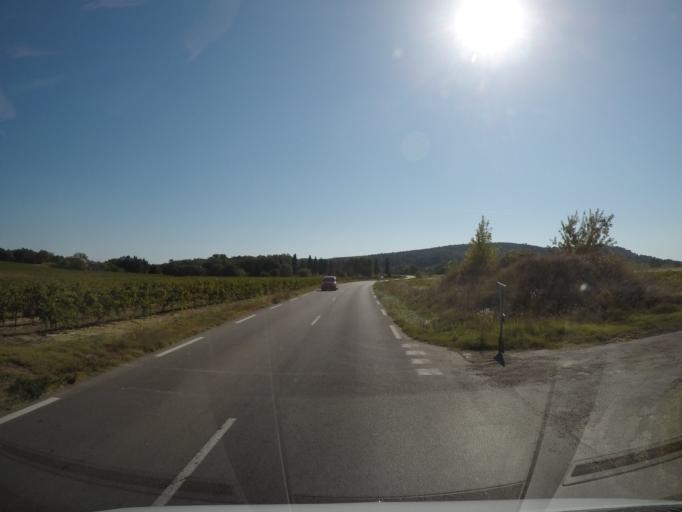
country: FR
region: Languedoc-Roussillon
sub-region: Departement du Gard
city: Ledignan
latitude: 44.0087
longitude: 4.1198
